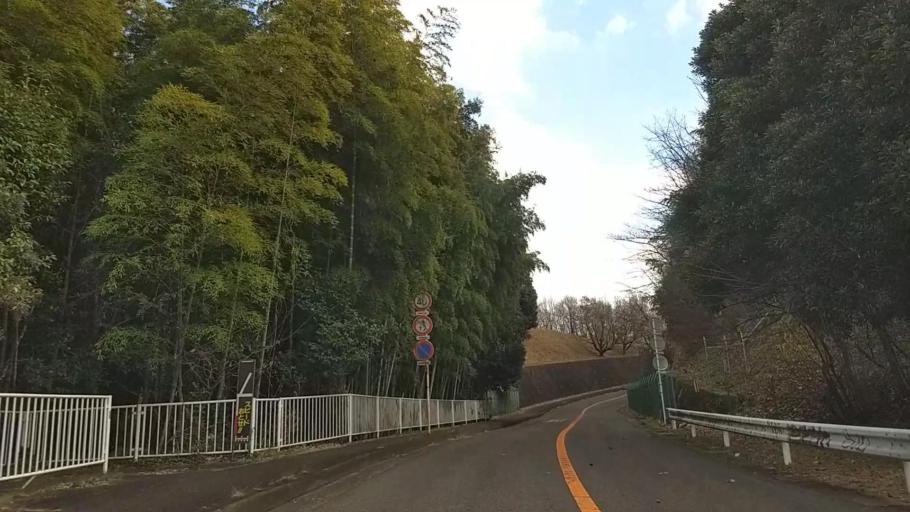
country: JP
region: Kanagawa
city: Isehara
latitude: 35.4299
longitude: 139.3104
